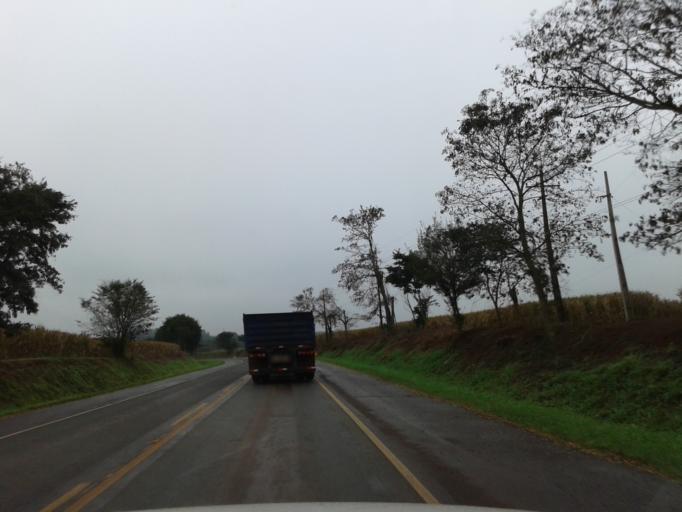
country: PY
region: Alto Parana
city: Naranjal
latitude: -25.9781
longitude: -55.1151
